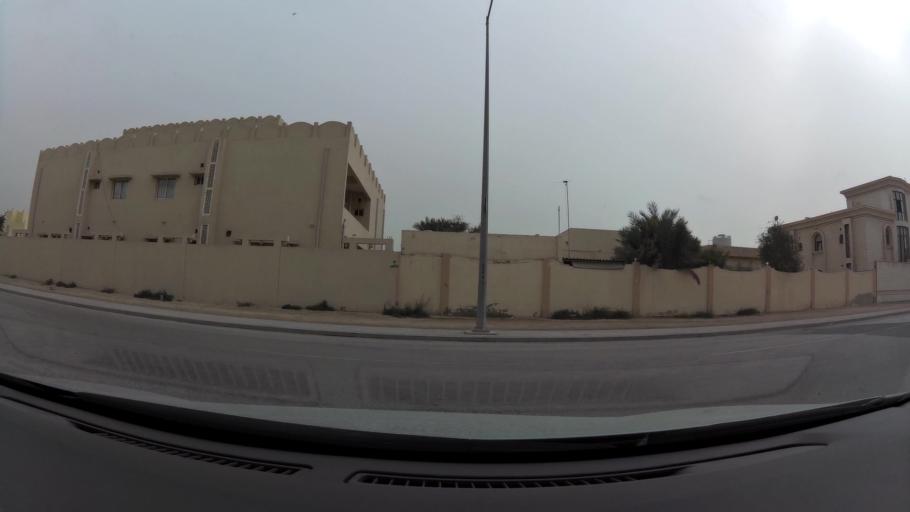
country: QA
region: Baladiyat ad Dawhah
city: Doha
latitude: 25.2463
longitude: 51.5197
